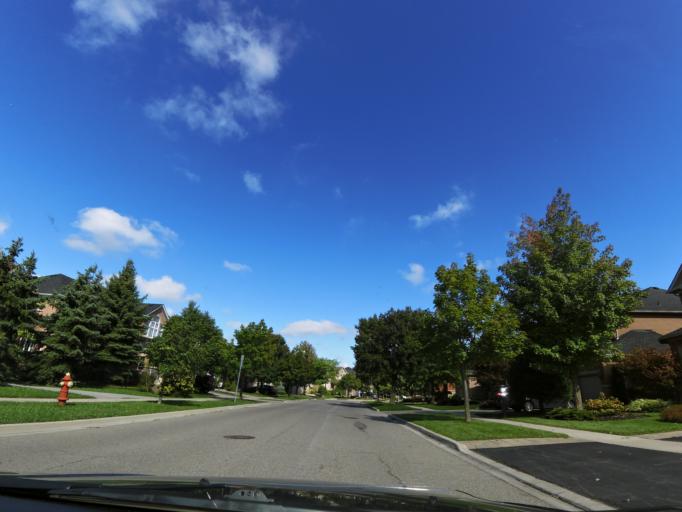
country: CA
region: Ontario
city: Burlington
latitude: 43.3966
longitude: -79.8067
